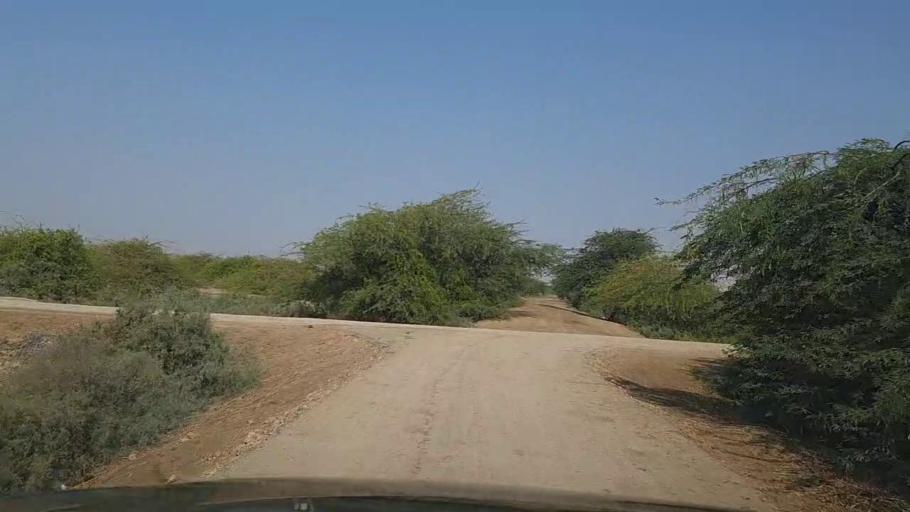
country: PK
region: Sindh
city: Thatta
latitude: 24.6493
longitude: 67.8170
